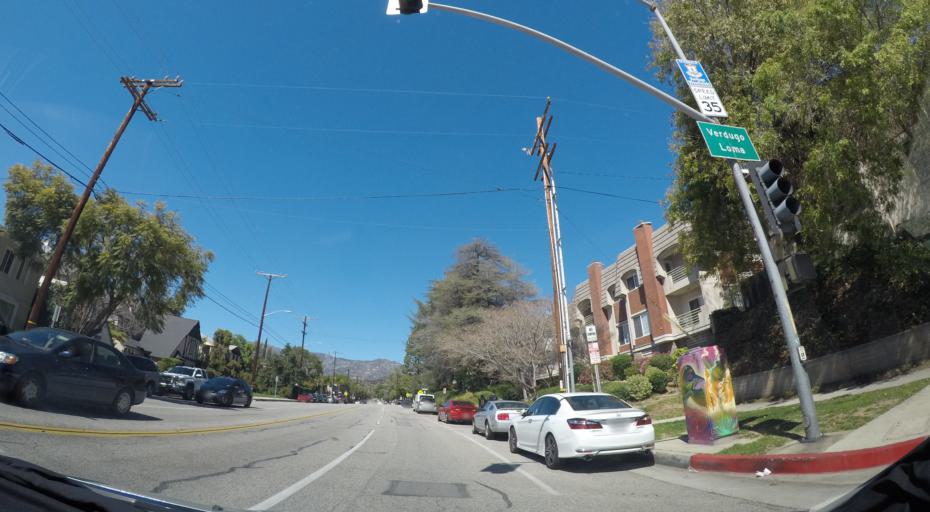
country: US
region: California
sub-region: Los Angeles County
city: North Glendale
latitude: 34.1704
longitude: -118.2272
